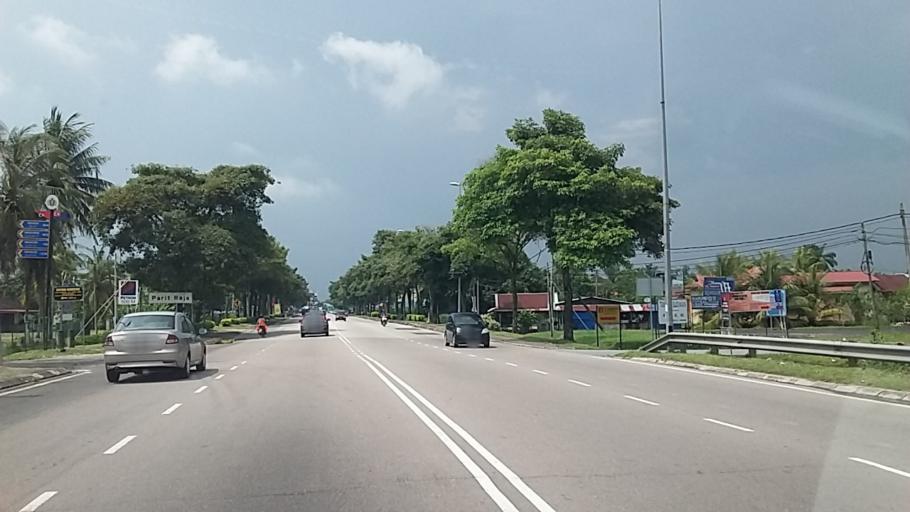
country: MY
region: Johor
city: Parit Raja
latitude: 1.8621
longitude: 103.1065
